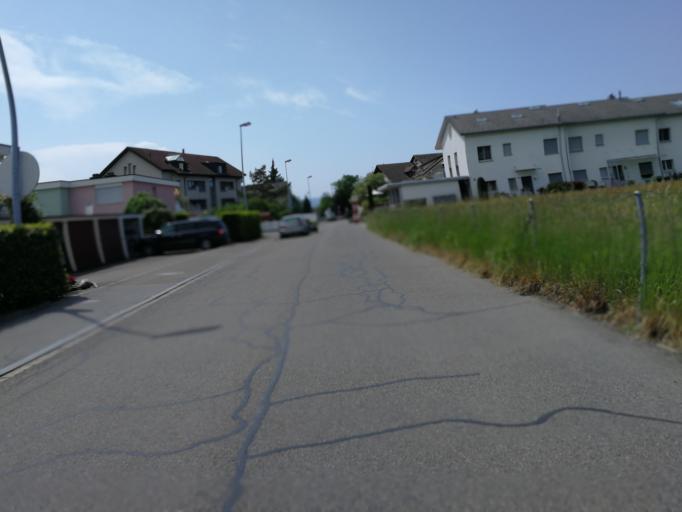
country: CH
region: Saint Gallen
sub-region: Wahlkreis See-Gaster
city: Rapperswil
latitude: 47.2360
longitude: 8.8220
